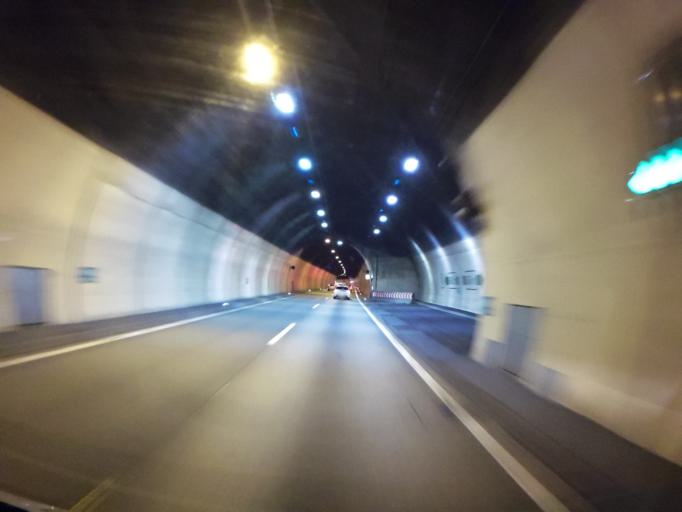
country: AT
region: Styria
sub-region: Politischer Bezirk Graz-Umgebung
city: Deutschfeistritz
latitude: 47.1947
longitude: 15.3251
